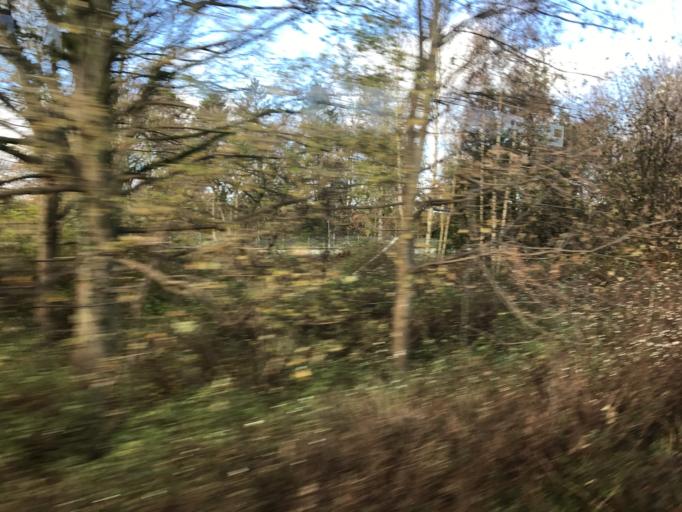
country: DK
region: Zealand
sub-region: Koge Kommune
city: Koge
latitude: 55.4490
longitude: 12.1843
